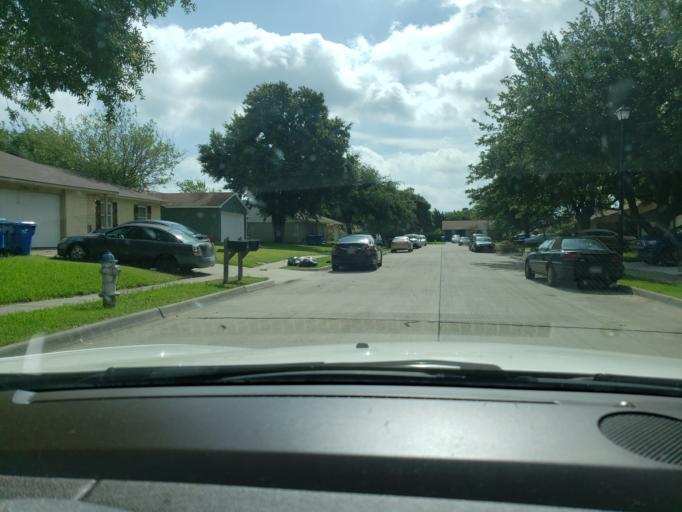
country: US
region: Texas
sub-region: Dallas County
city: Rowlett
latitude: 32.9114
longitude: -96.5722
